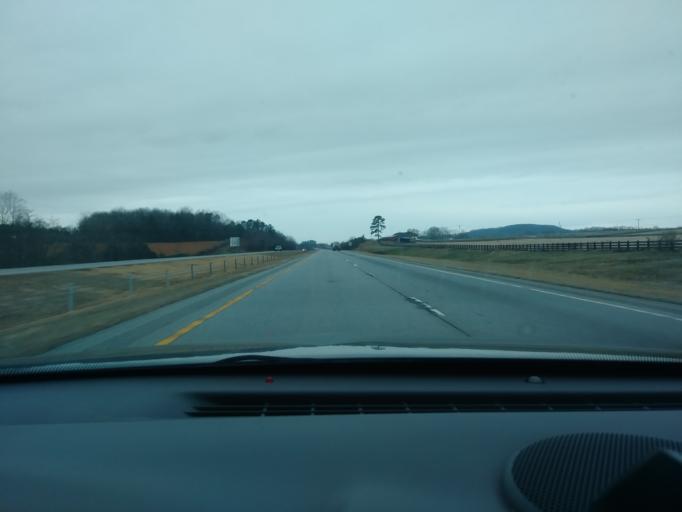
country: US
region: North Carolina
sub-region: Yadkin County
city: Jonesville
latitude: 36.1338
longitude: -80.8516
